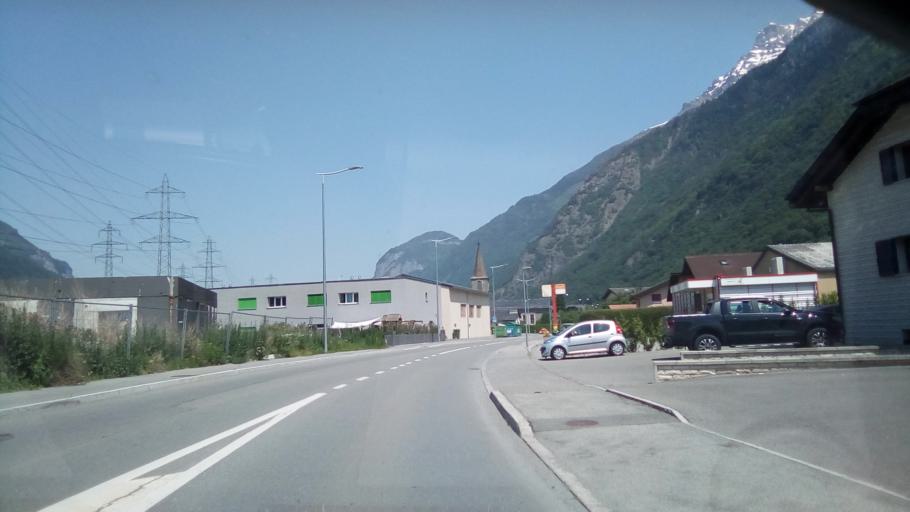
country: CH
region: Valais
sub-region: Saint-Maurice District
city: Vernayaz
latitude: 46.1470
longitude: 7.0420
